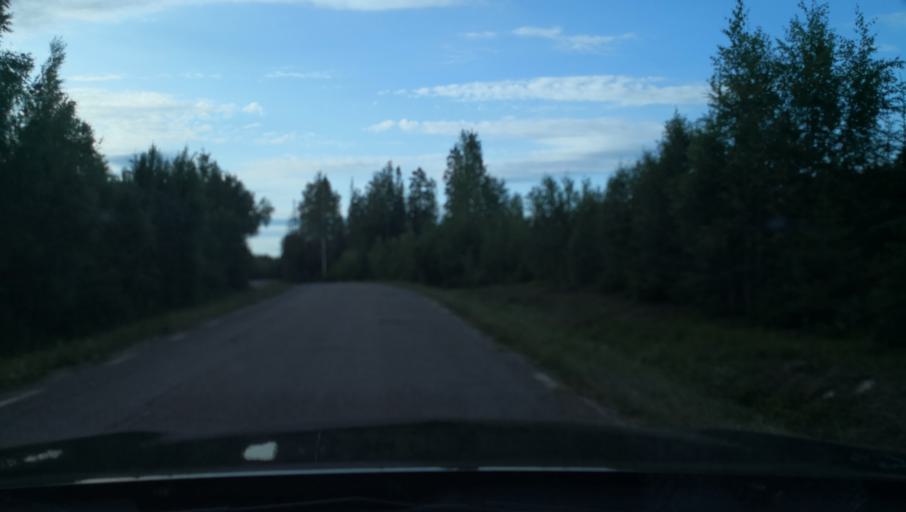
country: SE
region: Dalarna
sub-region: Ludvika Kommun
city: Ludvika
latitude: 60.1137
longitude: 15.2733
